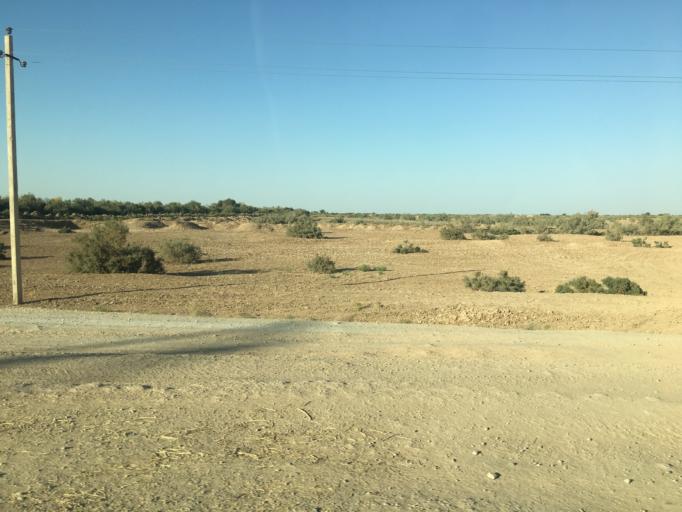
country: IR
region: Razavi Khorasan
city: Sarakhs
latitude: 37.0793
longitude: 61.2202
